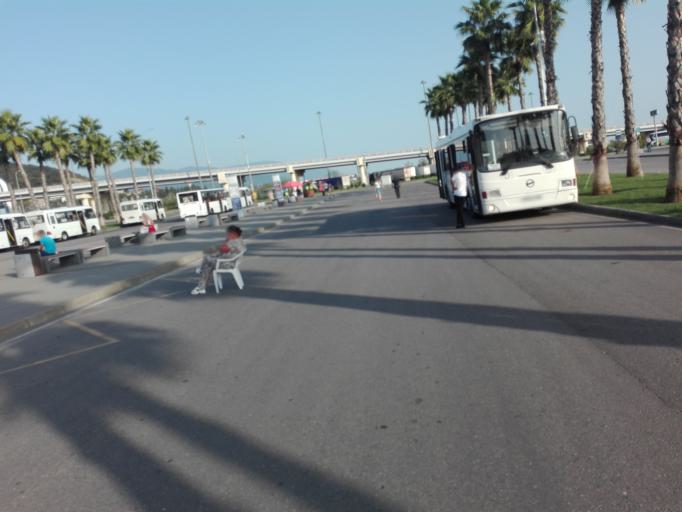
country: RU
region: Krasnodarskiy
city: Vysokoye
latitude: 43.4103
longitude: 39.9742
